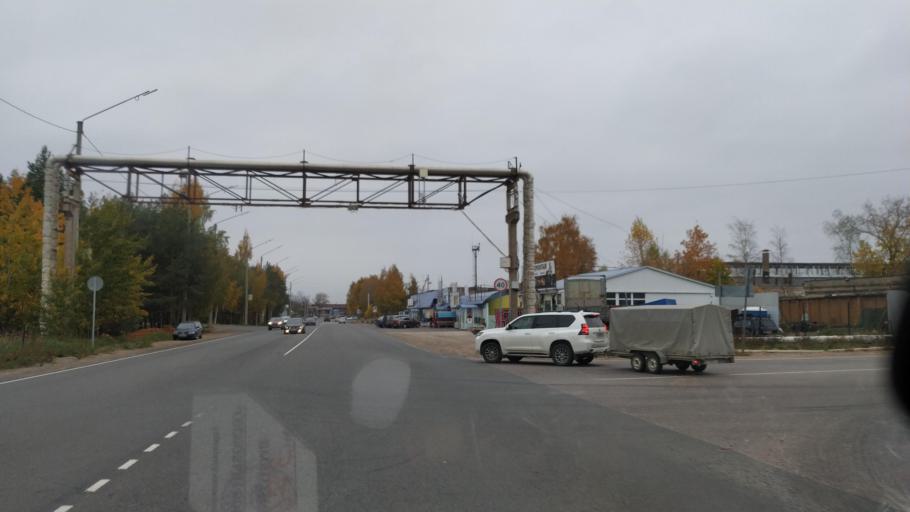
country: RU
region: Leningrad
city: Sosnovyy Bor
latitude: 59.8751
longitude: 29.0895
